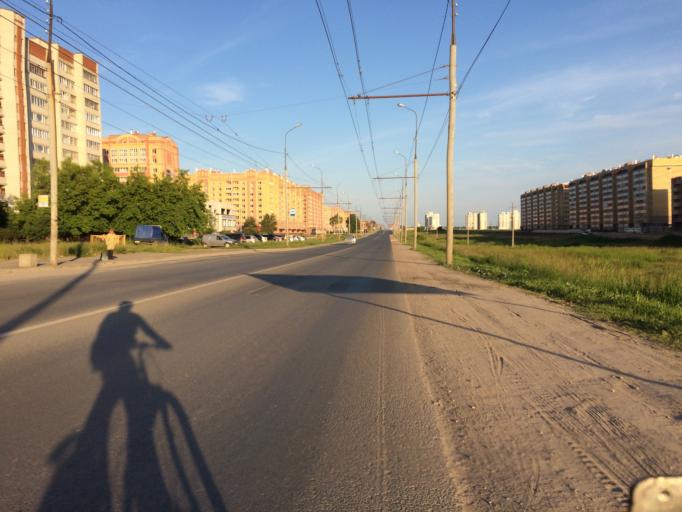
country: RU
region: Mariy-El
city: Medvedevo
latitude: 56.6401
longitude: 47.8278
